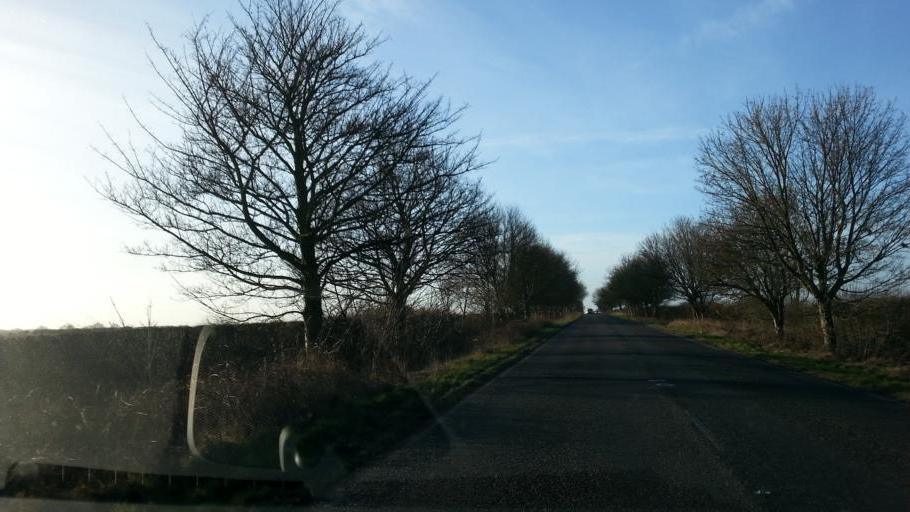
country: GB
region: England
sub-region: Lincolnshire
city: Grantham
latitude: 52.9286
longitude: -0.5708
